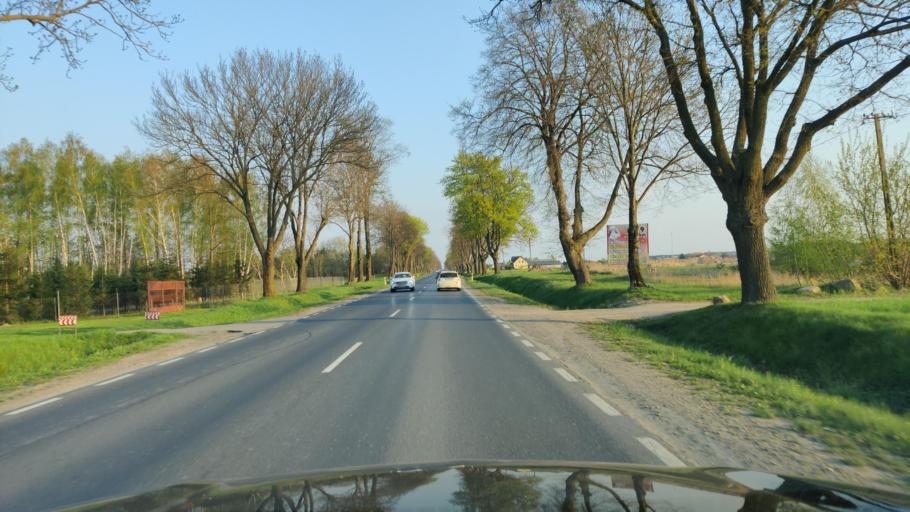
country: PL
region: Masovian Voivodeship
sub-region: Powiat pultuski
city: Pultusk
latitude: 52.6292
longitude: 21.0980
